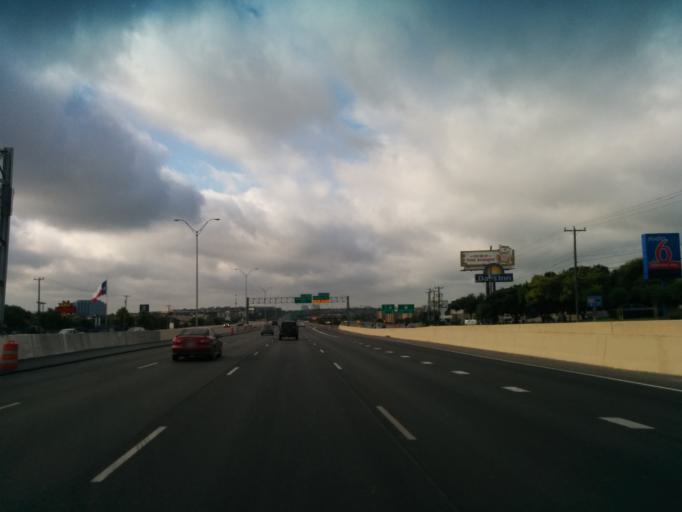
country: US
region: Texas
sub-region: Bexar County
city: Shavano Park
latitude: 29.5551
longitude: -98.5878
